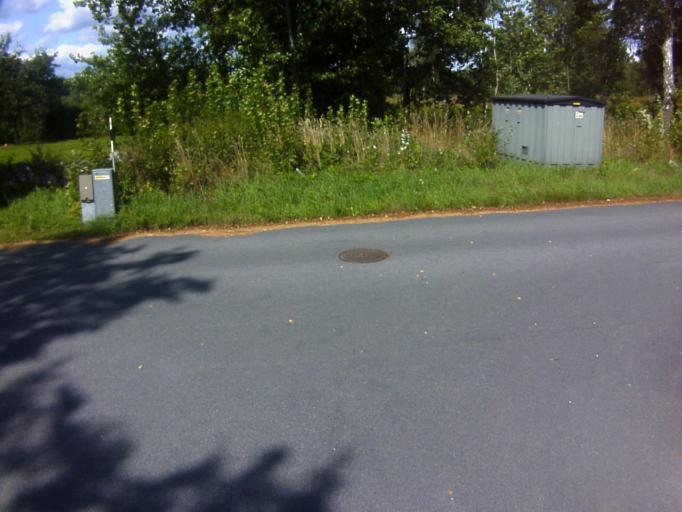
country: SE
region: Blekinge
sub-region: Karlshamns Kommun
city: Morrum
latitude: 56.1663
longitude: 14.6409
